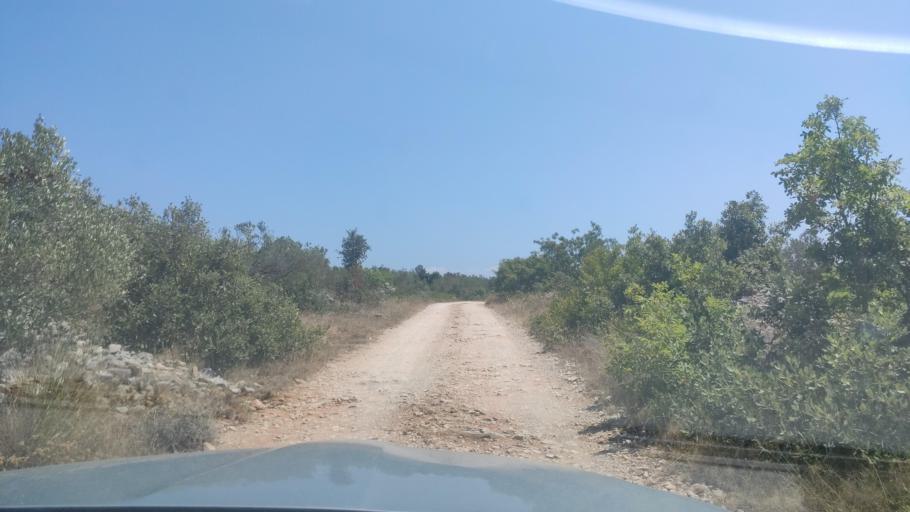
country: HR
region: Sibensko-Kniniska
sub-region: Grad Sibenik
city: Tisno
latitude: 43.7770
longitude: 15.6491
